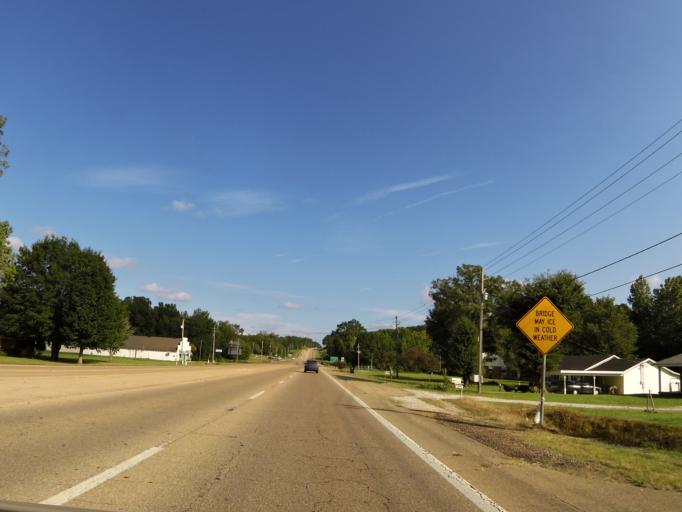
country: US
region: Mississippi
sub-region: Alcorn County
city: Farmington
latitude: 34.9023
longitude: -88.4802
